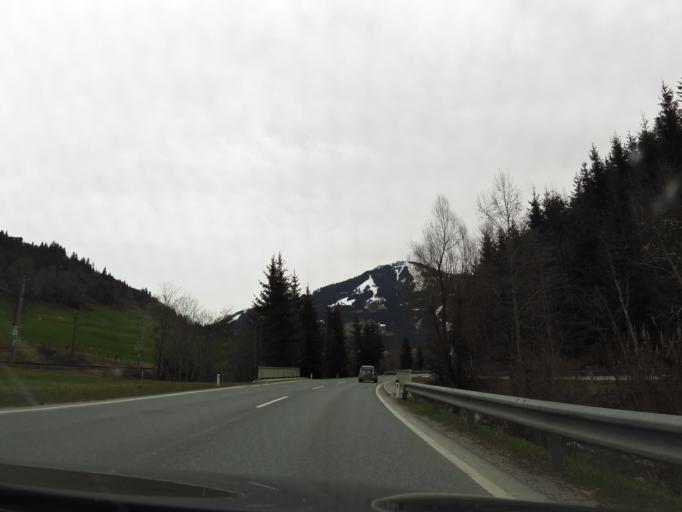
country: AT
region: Tyrol
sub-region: Politischer Bezirk Kitzbuhel
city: Westendorf
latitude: 47.4386
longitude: 12.1898
